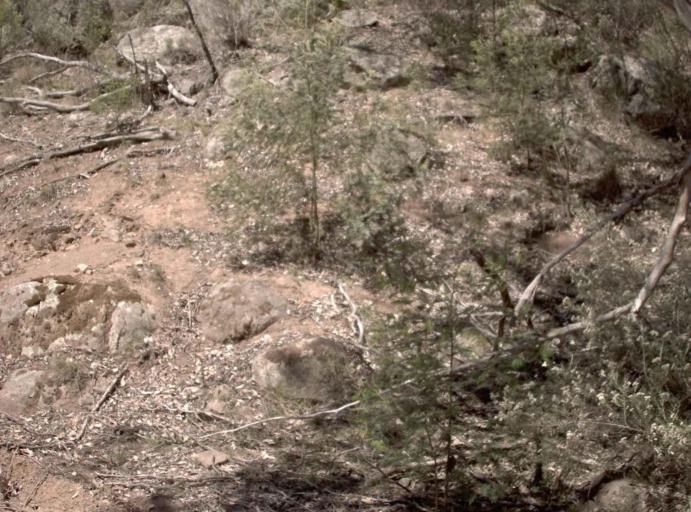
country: AU
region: New South Wales
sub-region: Snowy River
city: Jindabyne
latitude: -37.0549
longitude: 148.5371
